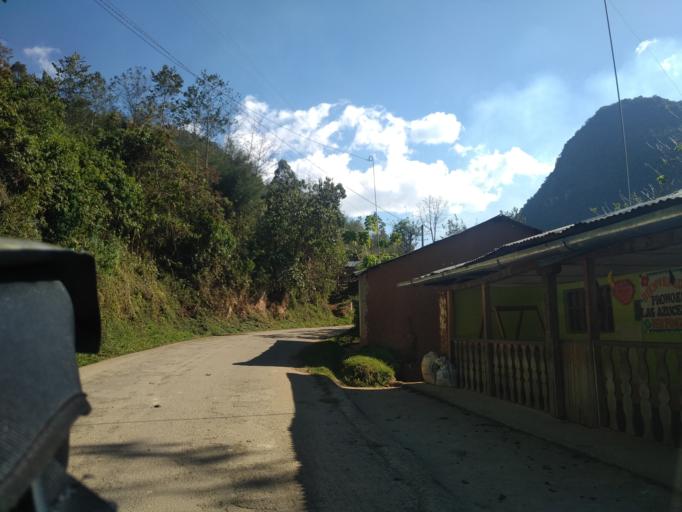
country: PE
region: Amazonas
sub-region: Provincia de Chachapoyas
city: Montevideo
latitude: -6.7185
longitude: -77.8213
